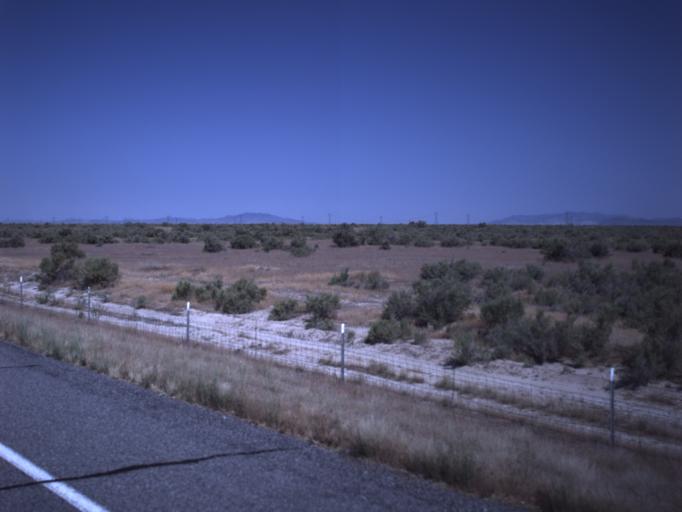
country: US
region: Utah
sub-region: Millard County
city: Delta
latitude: 39.4673
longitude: -112.4461
